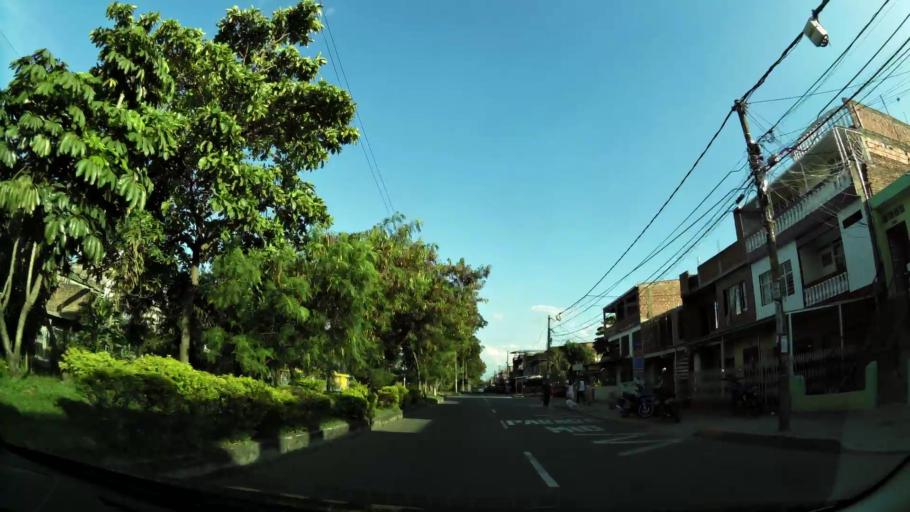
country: CO
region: Valle del Cauca
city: Cali
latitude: 3.4126
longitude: -76.5083
